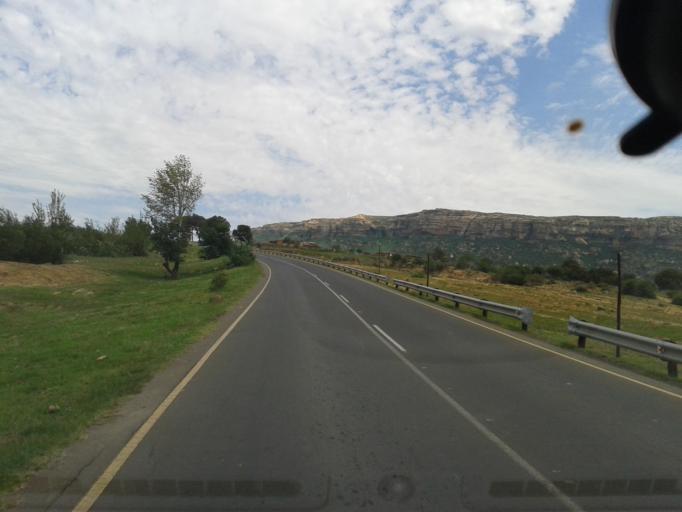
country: LS
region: Maseru
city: Maseru
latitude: -29.3500
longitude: 27.6091
